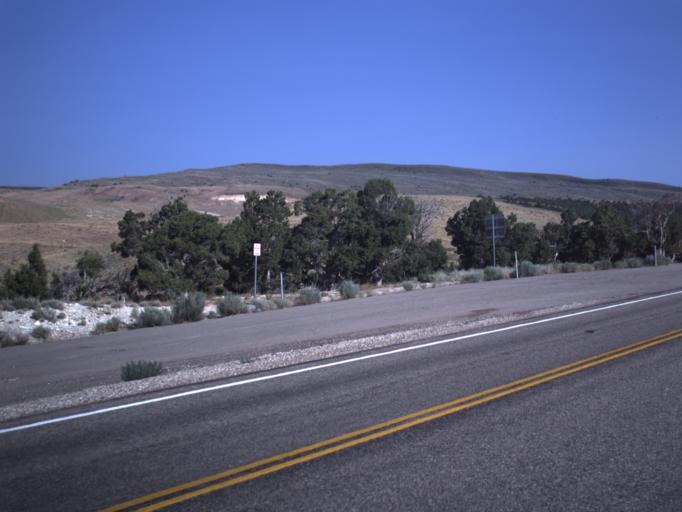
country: US
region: Utah
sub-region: Uintah County
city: Vernal
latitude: 40.6358
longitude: -109.4792
